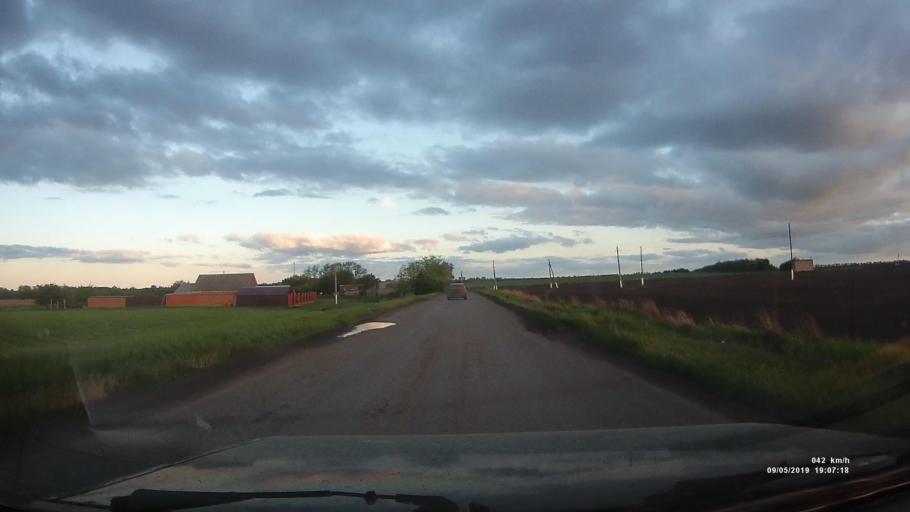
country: RU
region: Krasnodarskiy
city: Kanelovskaya
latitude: 46.7349
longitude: 39.1971
